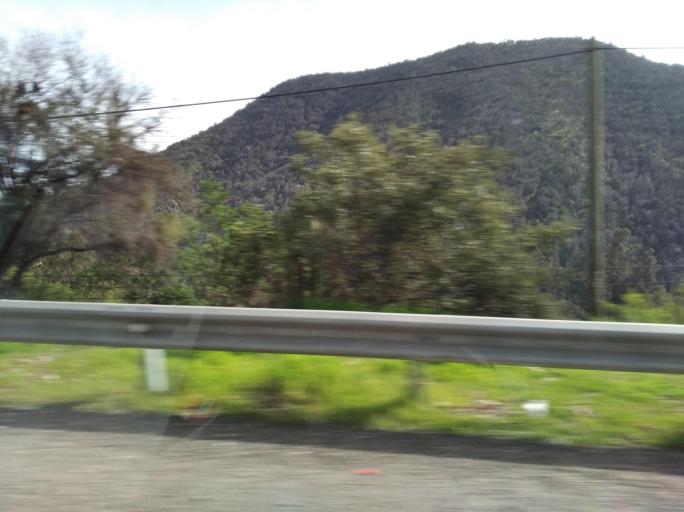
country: CL
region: Valparaiso
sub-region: Provincia de Marga Marga
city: Limache
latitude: -33.0631
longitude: -71.0642
